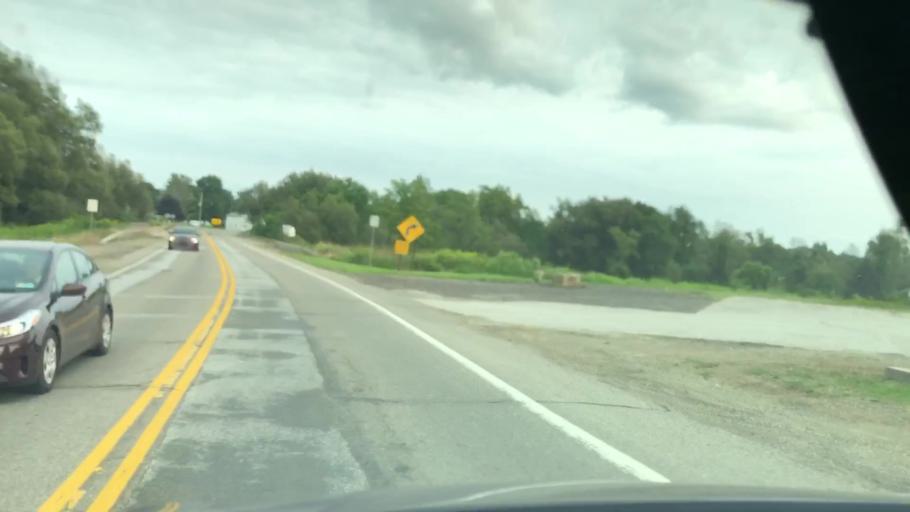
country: US
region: Pennsylvania
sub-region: Erie County
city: Union City
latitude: 42.0066
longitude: -79.8135
